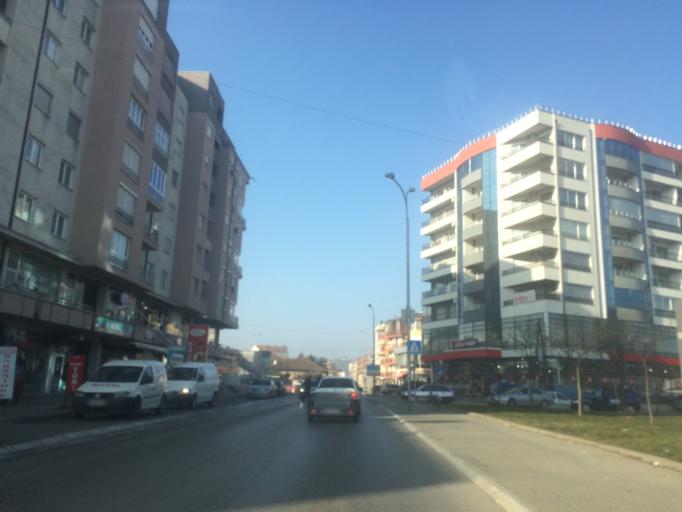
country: XK
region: Gjakova
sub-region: Komuna e Gjakoves
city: Gjakove
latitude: 42.3760
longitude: 20.4399
